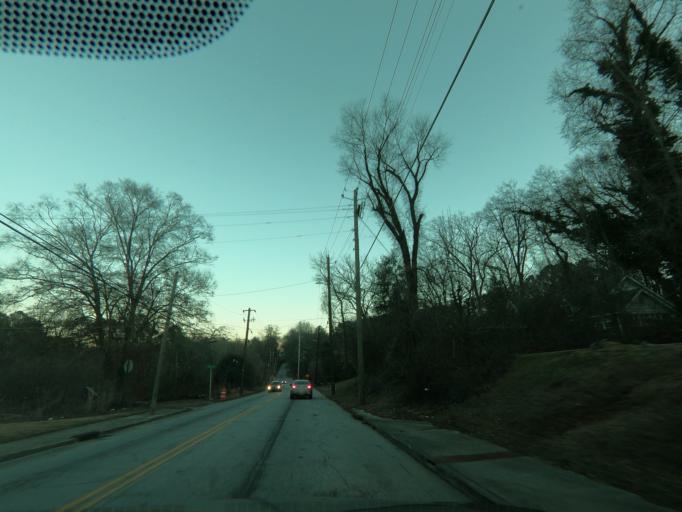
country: US
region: Georgia
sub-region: Cobb County
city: Vinings
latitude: 33.8175
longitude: -84.4609
